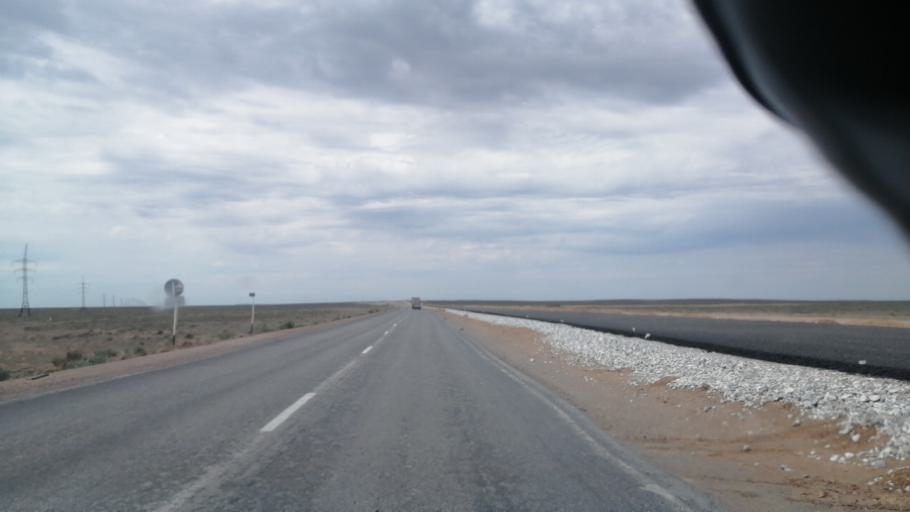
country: KZ
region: Qaraghandy
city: Saryshaghan
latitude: 46.5147
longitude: 74.1107
